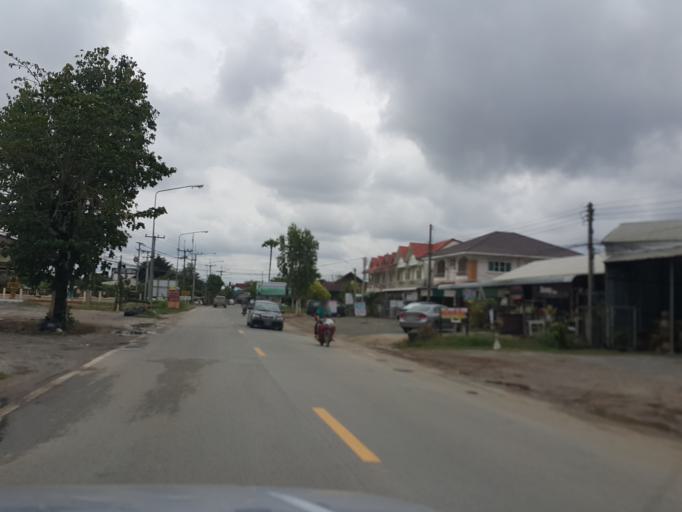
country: TH
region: Lamphun
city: Ban Thi
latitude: 18.5832
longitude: 99.0793
